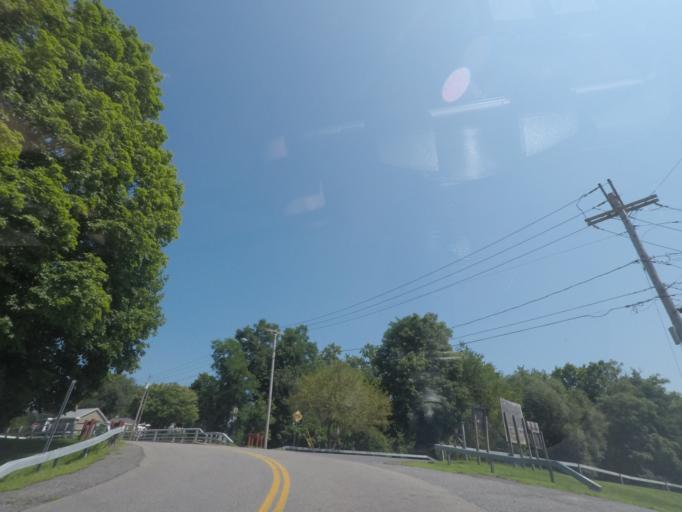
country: US
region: New York
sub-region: Saratoga County
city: Waterford
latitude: 42.7899
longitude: -73.6860
